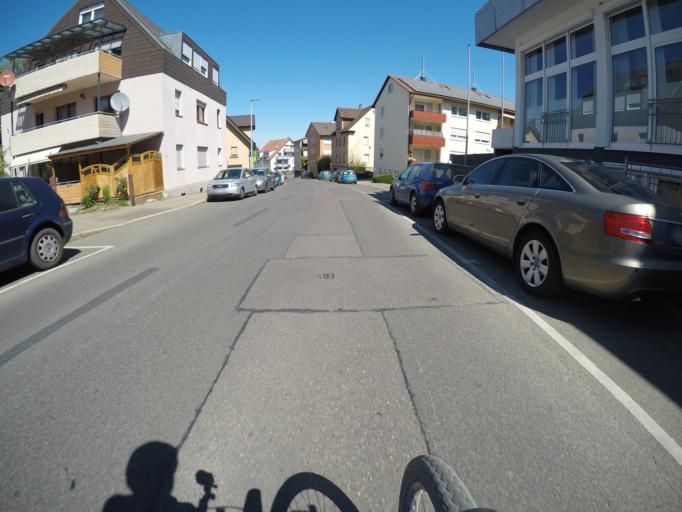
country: DE
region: Baden-Wuerttemberg
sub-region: Regierungsbezirk Stuttgart
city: Waiblingen
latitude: 48.8269
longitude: 9.3144
